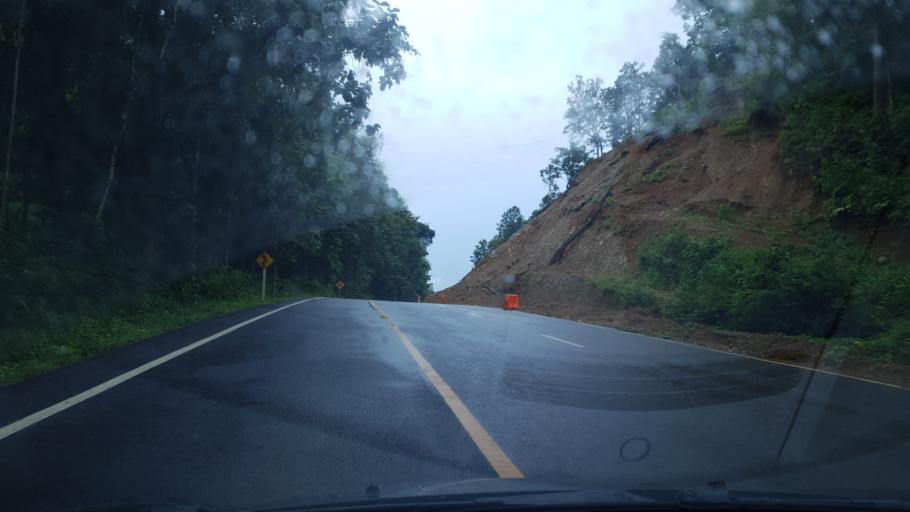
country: TH
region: Mae Hong Son
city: Pa Pae
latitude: 18.2660
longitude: 97.9427
